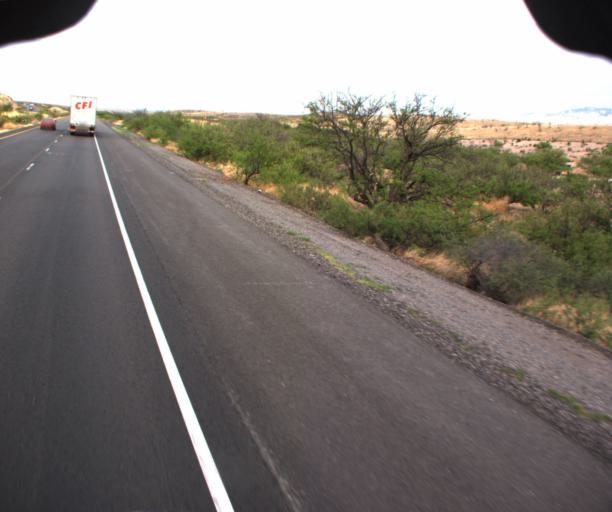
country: US
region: Arizona
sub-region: Cochise County
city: Mescal
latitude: 31.9660
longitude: -110.4615
